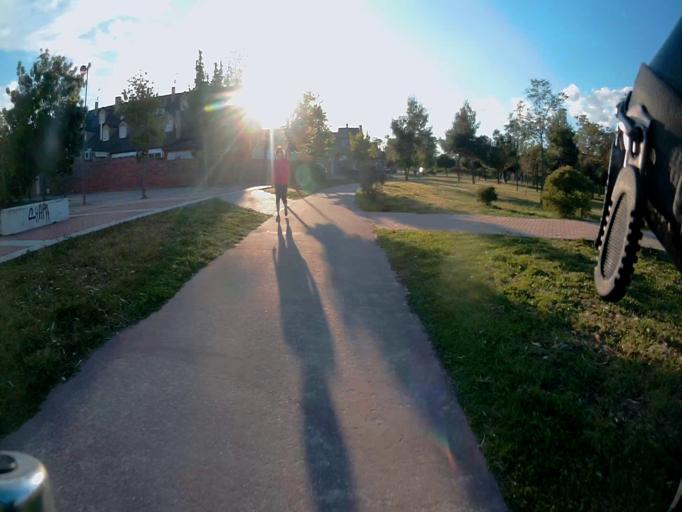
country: ES
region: Madrid
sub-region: Provincia de Madrid
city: Fuenlabrada
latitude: 40.3117
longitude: -3.7896
